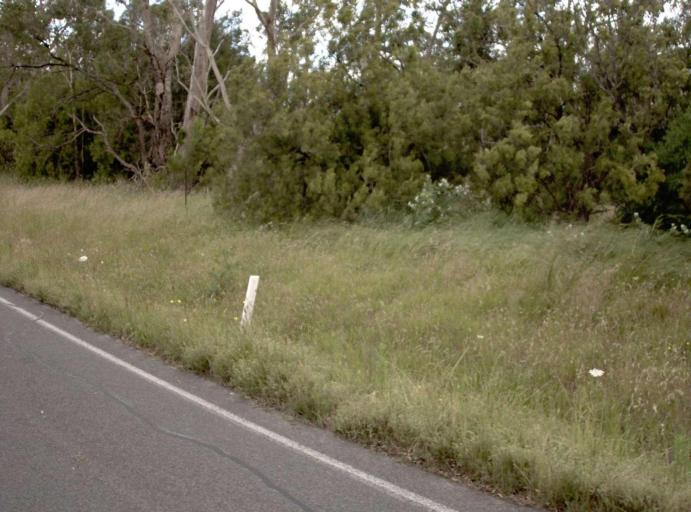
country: AU
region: Victoria
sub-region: Latrobe
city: Moe
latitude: -38.1275
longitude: 146.2555
